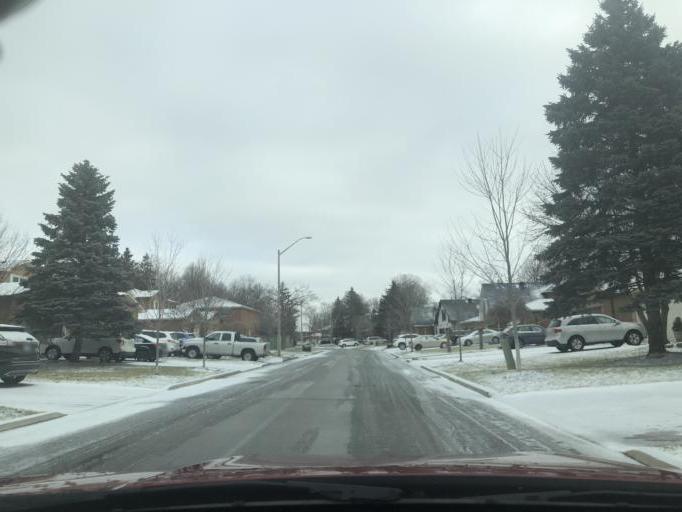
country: CA
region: Ontario
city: Markham
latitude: 43.8712
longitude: -79.2381
